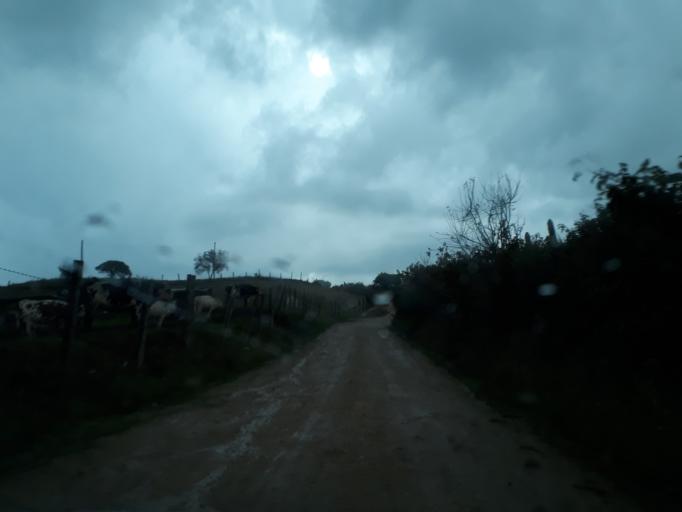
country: CO
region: Cundinamarca
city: Villapinzon
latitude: 5.2964
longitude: -73.6091
